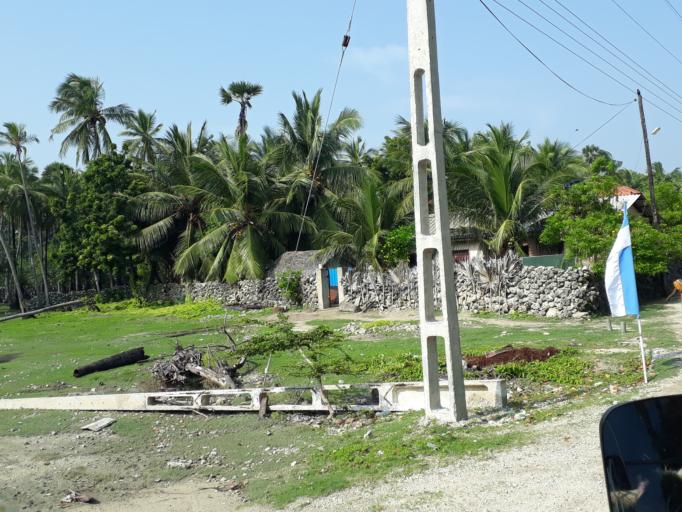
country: LK
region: Northern Province
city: Jaffna
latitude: 9.5278
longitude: 79.7147
